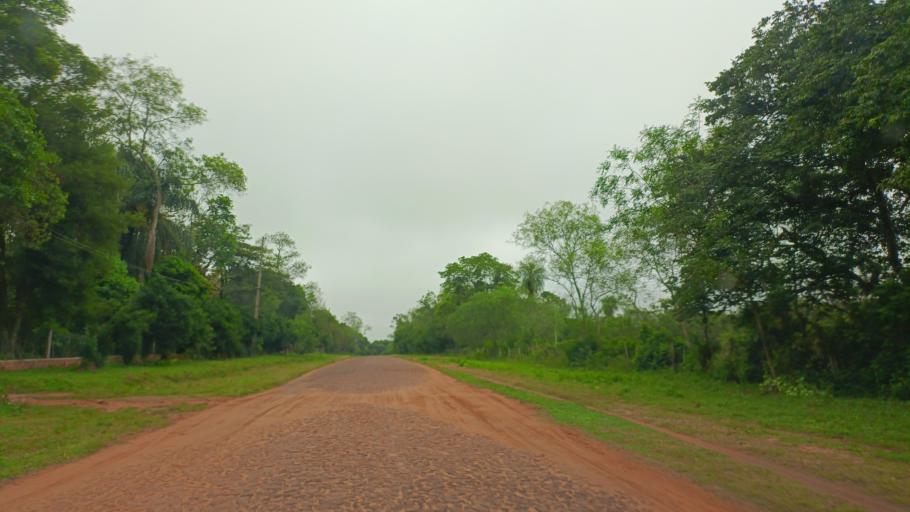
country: PY
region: Misiones
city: Santa Maria
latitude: -26.8680
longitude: -57.0113
